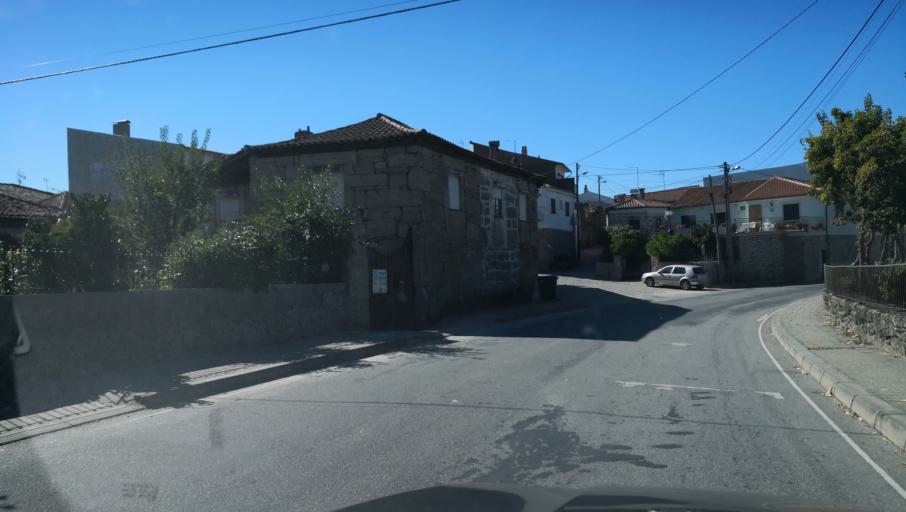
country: PT
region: Vila Real
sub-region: Valpacos
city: Valpacos
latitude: 41.6618
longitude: -7.3187
